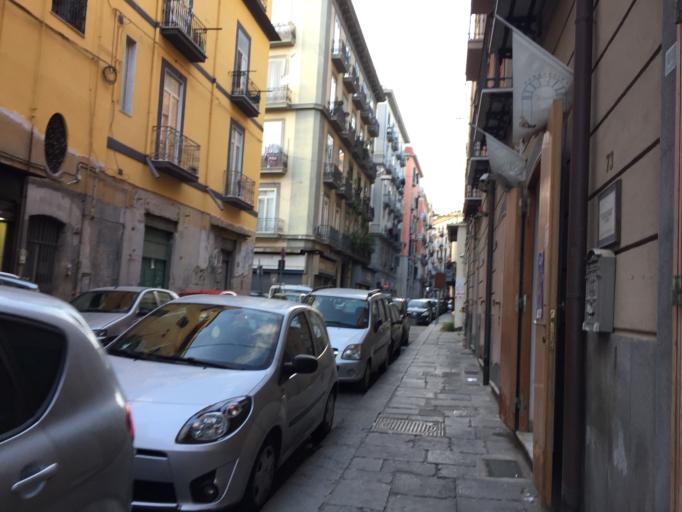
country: IT
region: Campania
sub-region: Provincia di Napoli
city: Napoli
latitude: 40.8466
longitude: 14.2638
